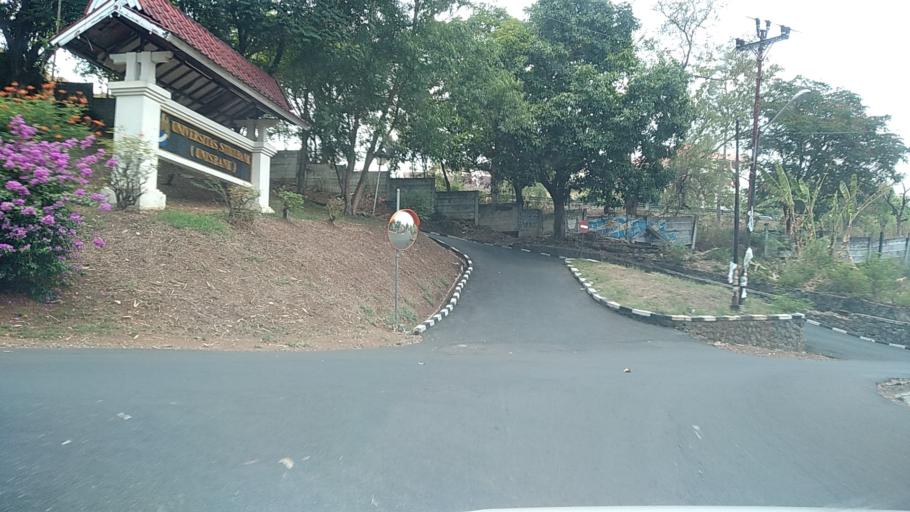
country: ID
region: Central Java
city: Semarang
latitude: -7.0167
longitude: 110.3963
